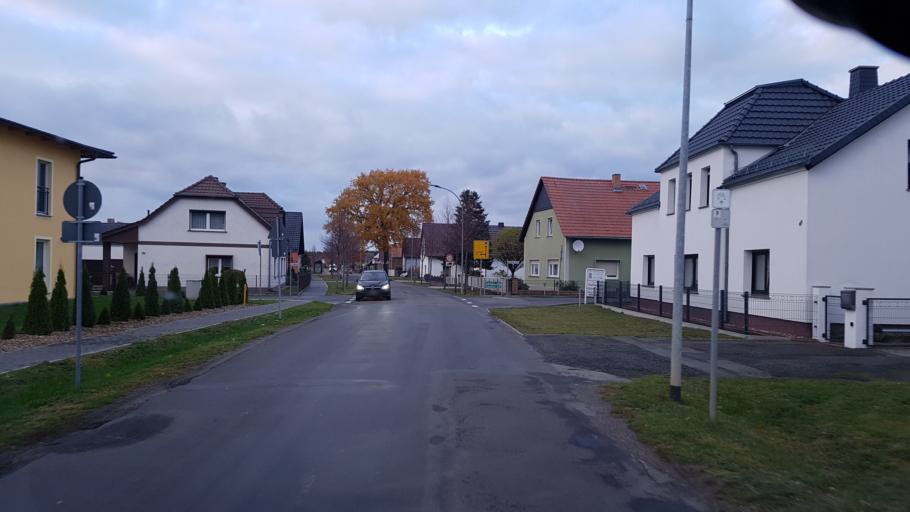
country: DE
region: Brandenburg
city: Lindenau
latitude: 51.4143
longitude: 13.7704
